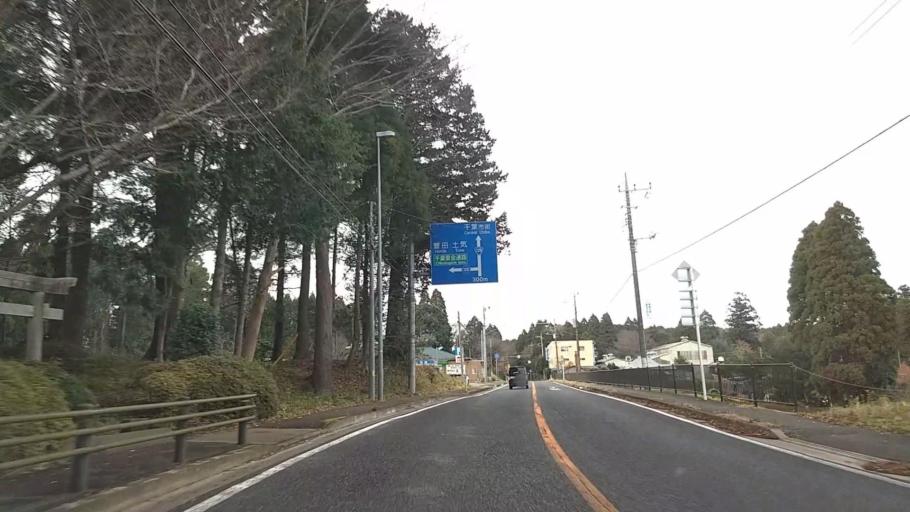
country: JP
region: Chiba
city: Oami
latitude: 35.5788
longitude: 140.2648
